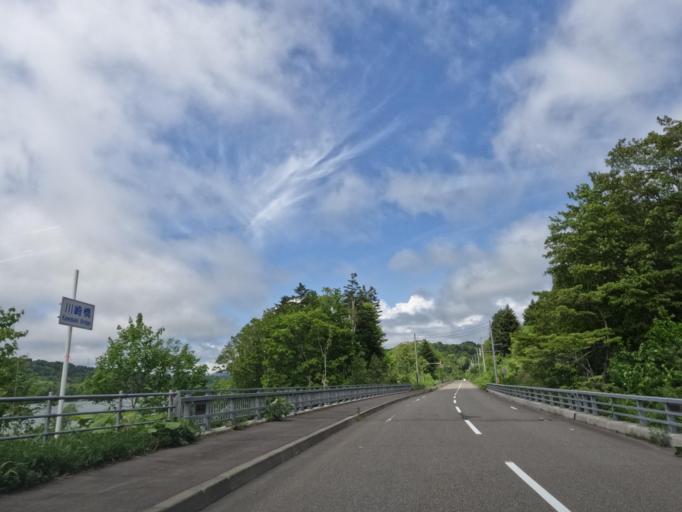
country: JP
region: Hokkaido
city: Tobetsu
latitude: 43.3500
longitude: 141.5675
